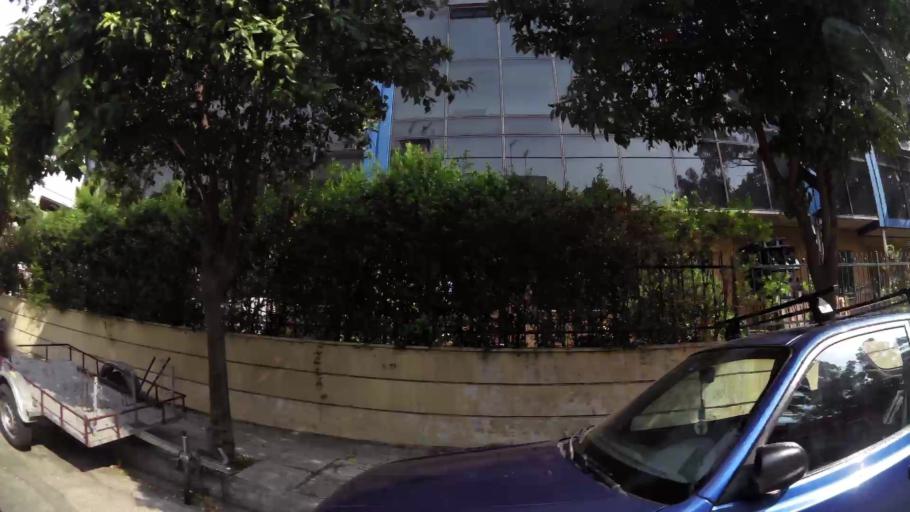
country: GR
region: Attica
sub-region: Nomos Piraios
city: Agios Ioannis Rentis
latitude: 37.9494
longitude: 23.6624
